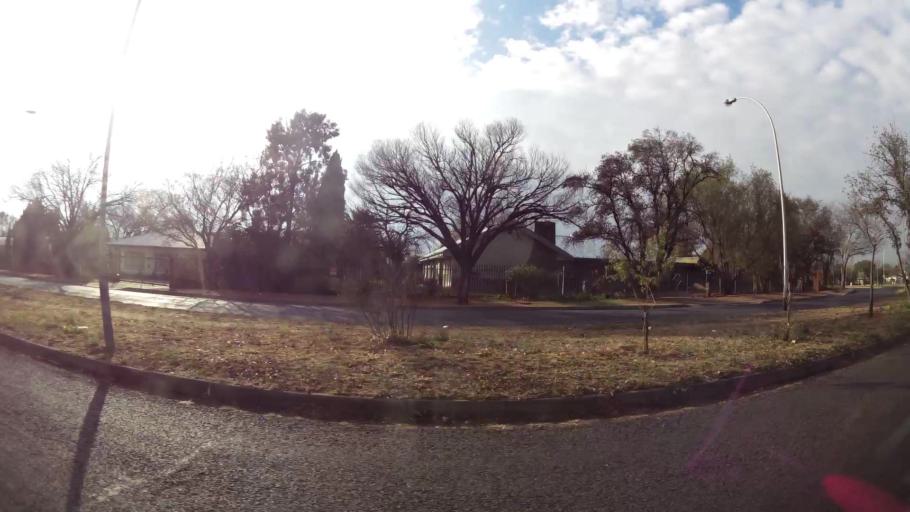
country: ZA
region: Orange Free State
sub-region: Mangaung Metropolitan Municipality
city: Bloemfontein
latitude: -29.1223
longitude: 26.1738
